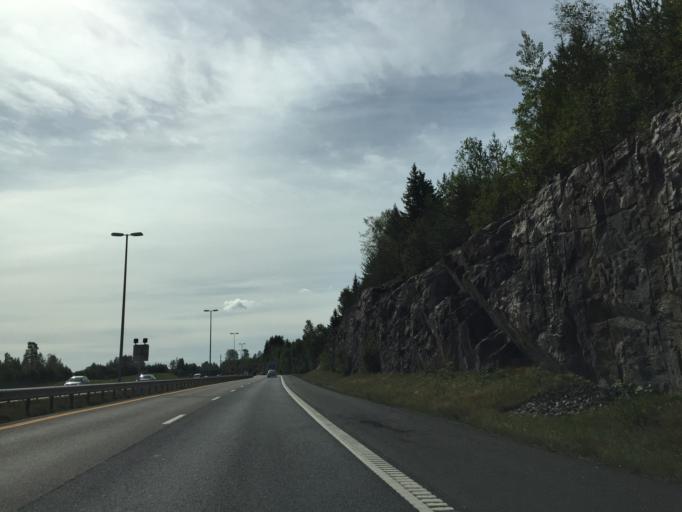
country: NO
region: Akershus
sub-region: As
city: As
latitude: 59.6868
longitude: 10.7366
